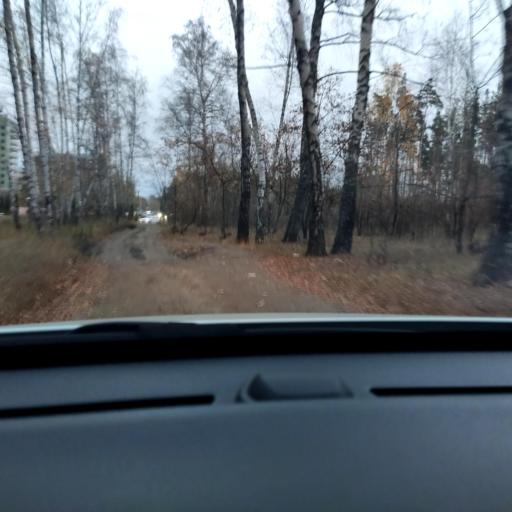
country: RU
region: Voronezj
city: Somovo
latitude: 51.6844
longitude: 39.2854
